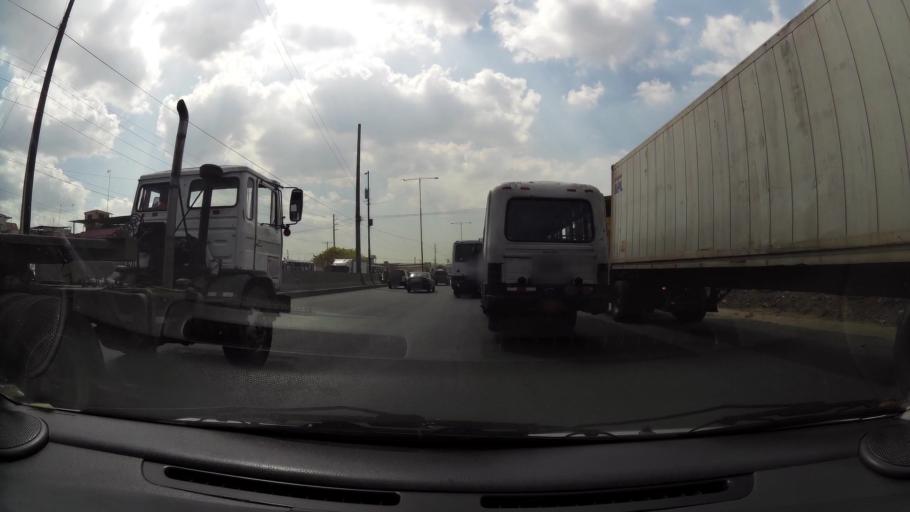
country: EC
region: Guayas
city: Santa Lucia
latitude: -2.1282
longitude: -79.9493
